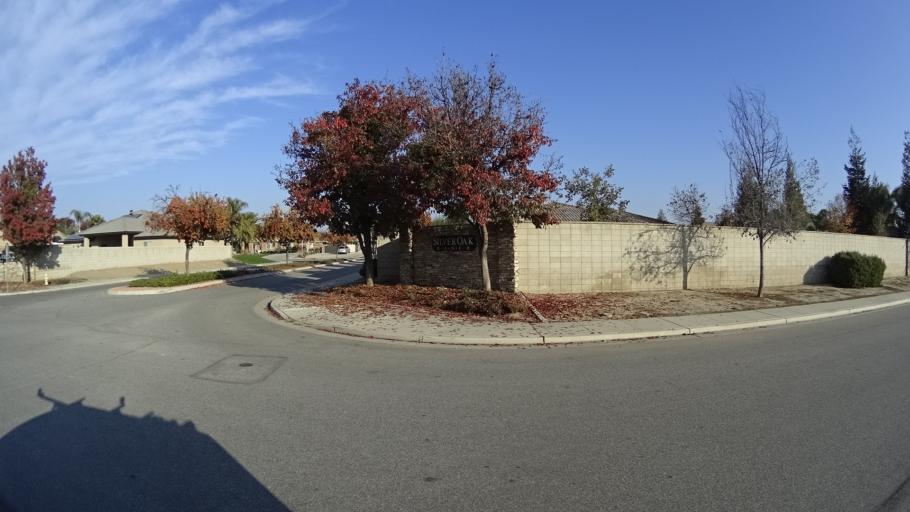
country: US
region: California
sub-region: Kern County
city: Rosedale
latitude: 35.3690
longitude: -119.1750
